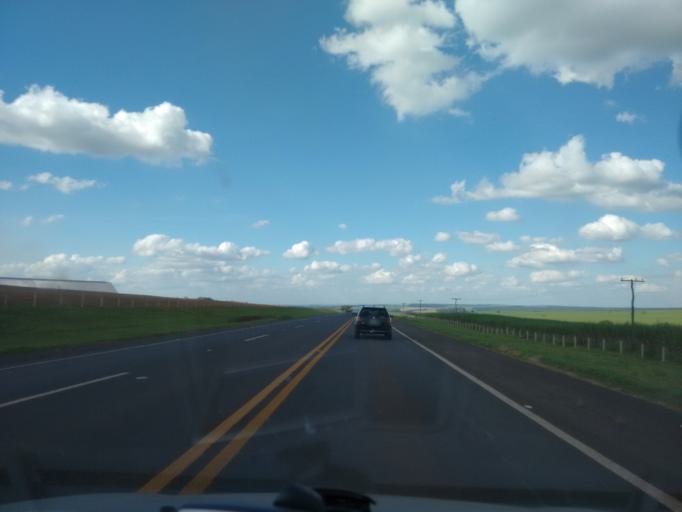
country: BR
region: Sao Paulo
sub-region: Americo Brasiliense
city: Americo Brasiliense
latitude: -21.7660
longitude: -48.0853
